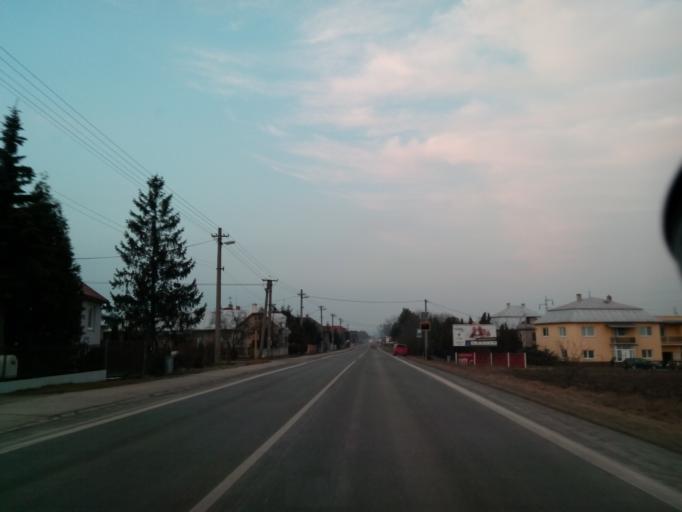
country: SK
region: Kosicky
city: Kosice
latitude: 48.6527
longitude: 21.2701
